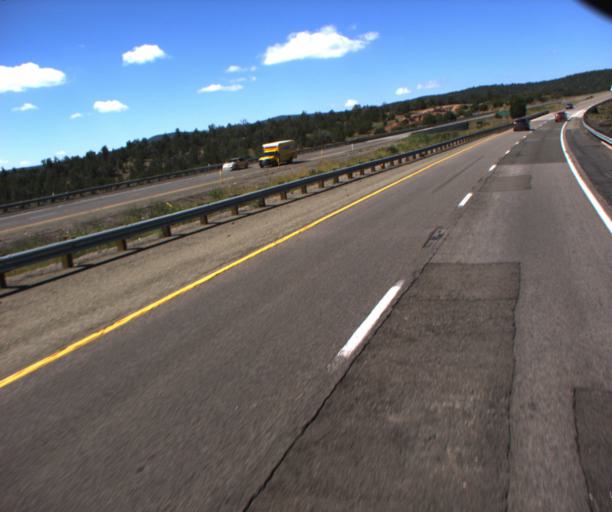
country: US
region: Arizona
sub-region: Mohave County
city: Peach Springs
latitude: 35.2944
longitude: -113.0301
